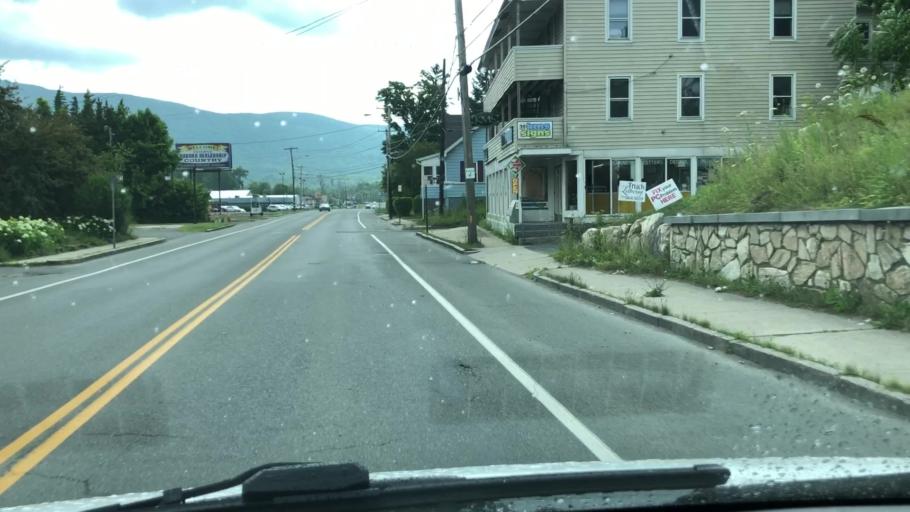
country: US
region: Massachusetts
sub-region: Berkshire County
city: North Adams
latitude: 42.6904
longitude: -73.1132
